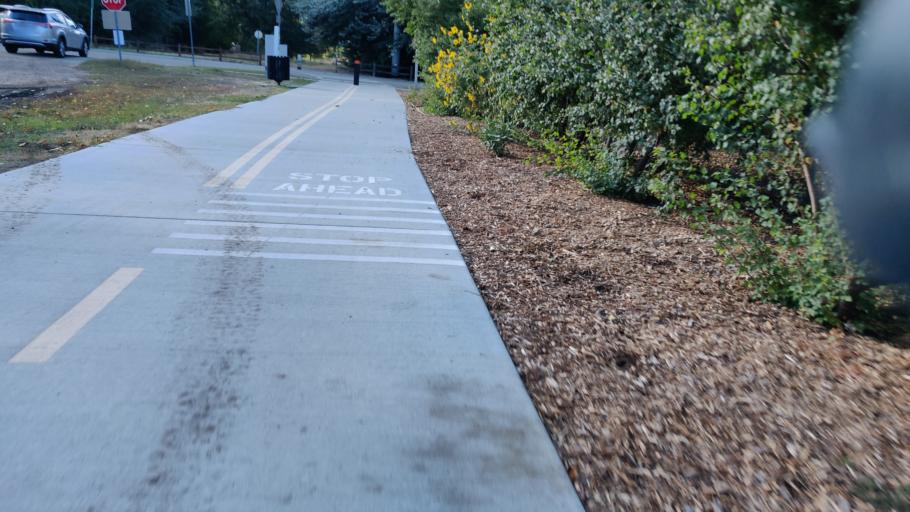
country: US
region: Idaho
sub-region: Ada County
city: Boise
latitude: 43.6041
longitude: -116.1844
